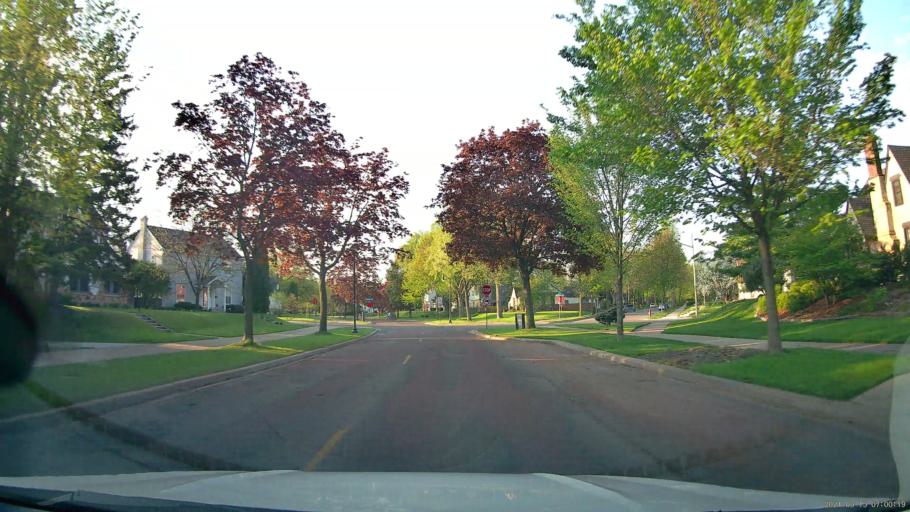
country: US
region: Minnesota
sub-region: Hennepin County
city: Saint Anthony
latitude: 45.0209
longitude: -93.2321
